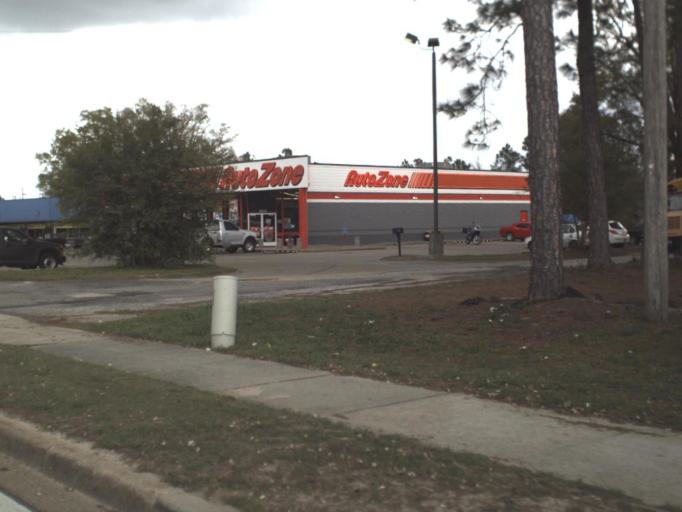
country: US
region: Florida
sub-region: Okaloosa County
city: Crestview
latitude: 30.7383
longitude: -86.5647
